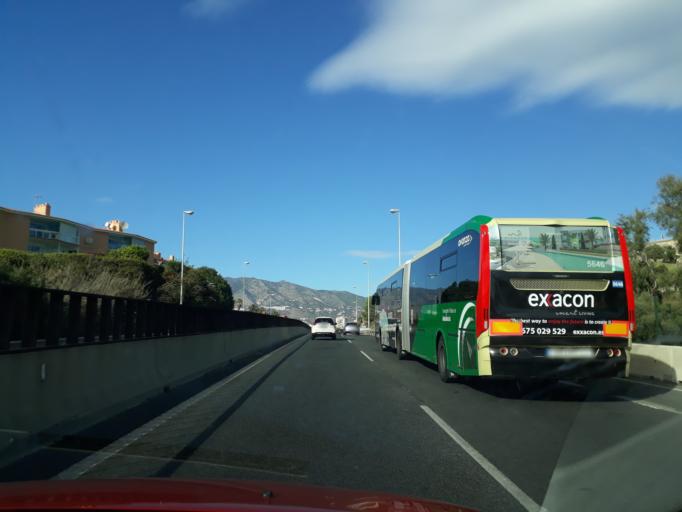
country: ES
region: Andalusia
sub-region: Provincia de Malaga
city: Fuengirola
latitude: 36.5238
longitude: -4.6302
